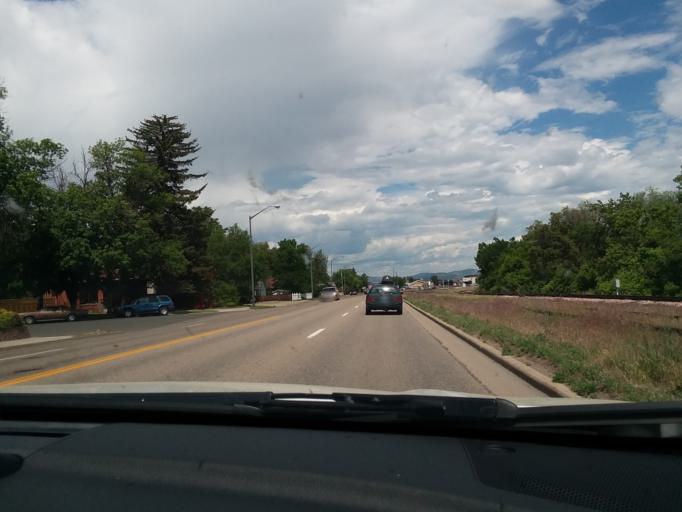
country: US
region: Colorado
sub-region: Larimer County
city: Fort Collins
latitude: 40.5847
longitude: -105.0679
